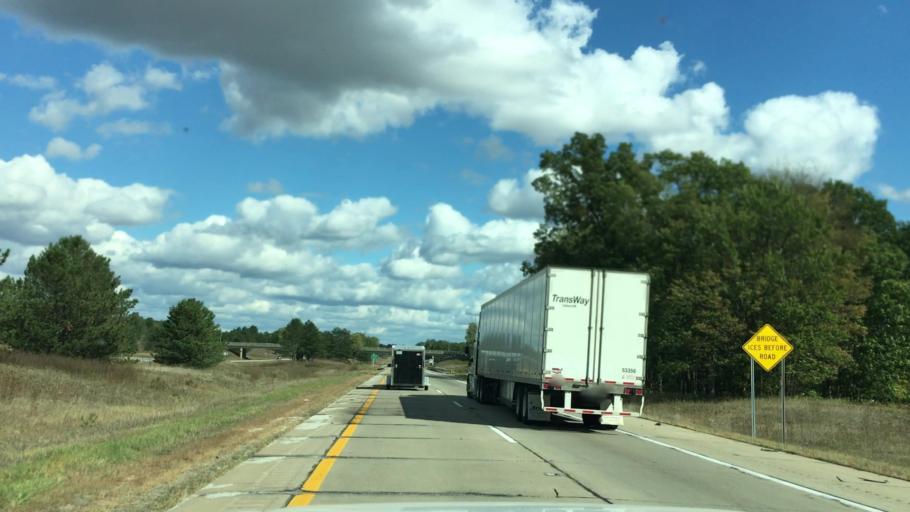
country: US
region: Michigan
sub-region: Eaton County
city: Olivet
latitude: 42.4575
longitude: -84.9325
